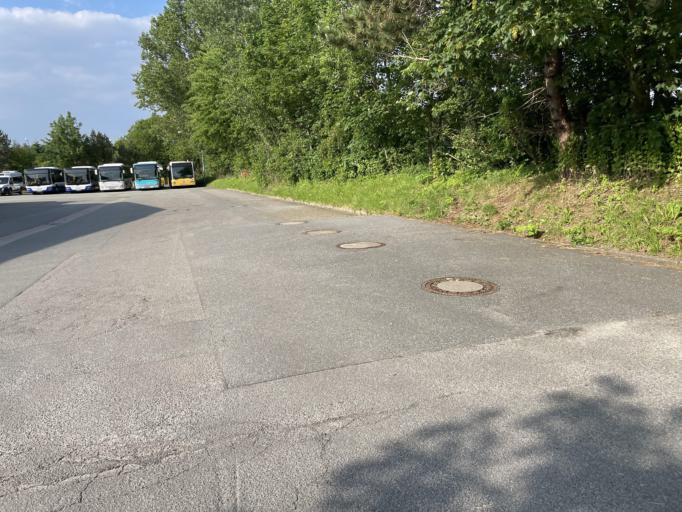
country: DE
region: Schleswig-Holstein
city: Husum
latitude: 54.4697
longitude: 9.0683
